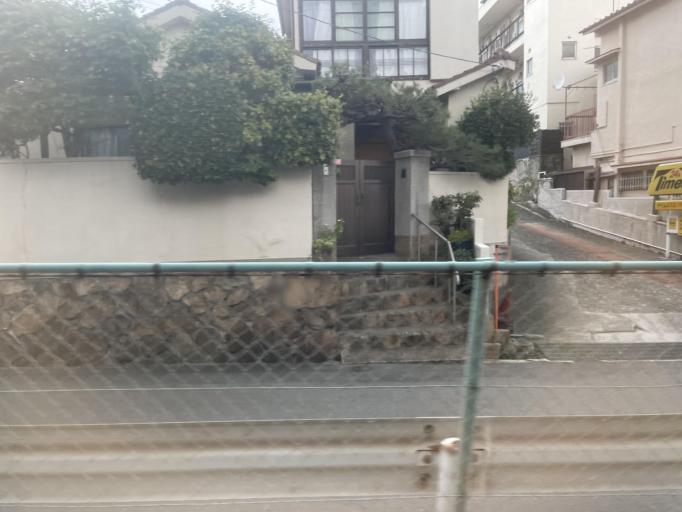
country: JP
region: Hyogo
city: Kobe
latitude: 34.7208
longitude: 135.2369
